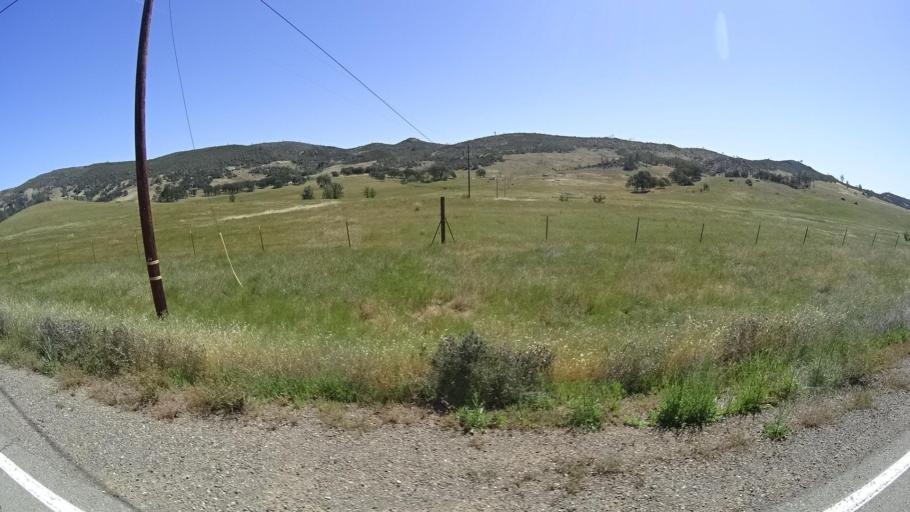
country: US
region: California
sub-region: Lake County
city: Hidden Valley Lake
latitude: 38.8634
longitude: -122.4123
